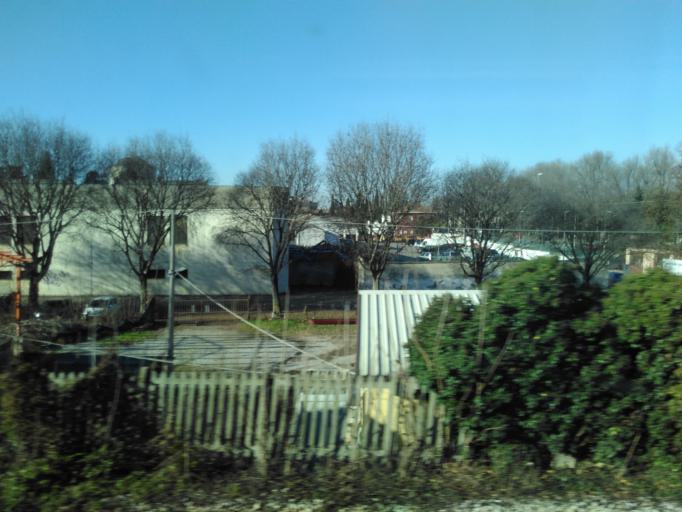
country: IT
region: Veneto
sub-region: Provincia di Verona
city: Verona
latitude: 45.4328
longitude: 11.0093
